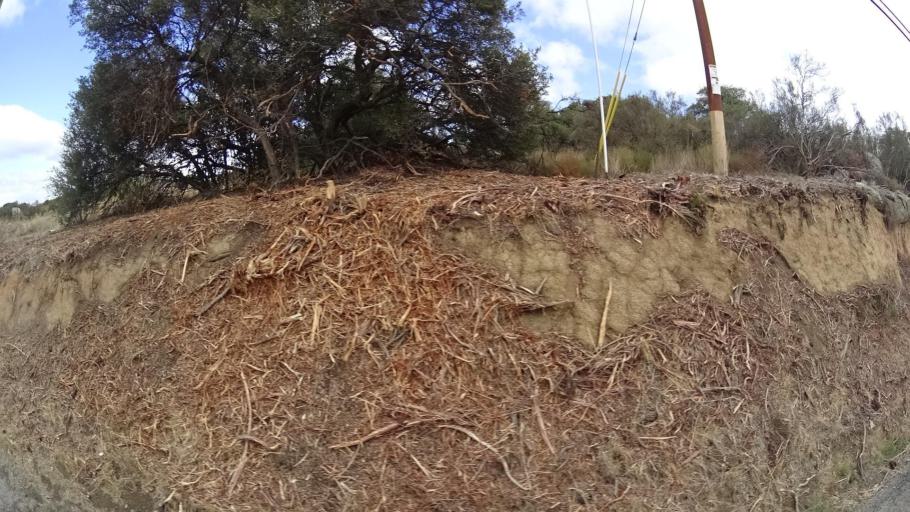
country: US
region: California
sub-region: San Diego County
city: Campo
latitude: 32.6728
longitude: -116.5045
